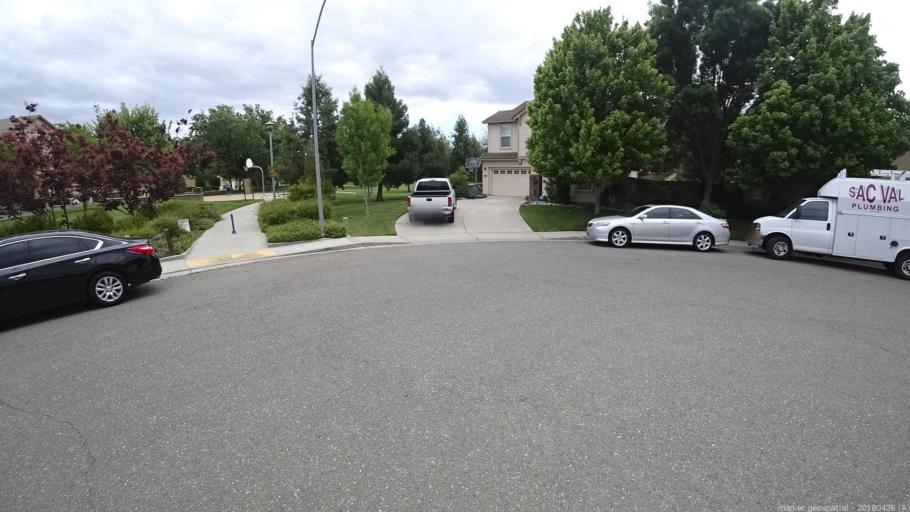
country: US
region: California
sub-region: Yolo County
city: West Sacramento
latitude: 38.5534
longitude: -121.5194
